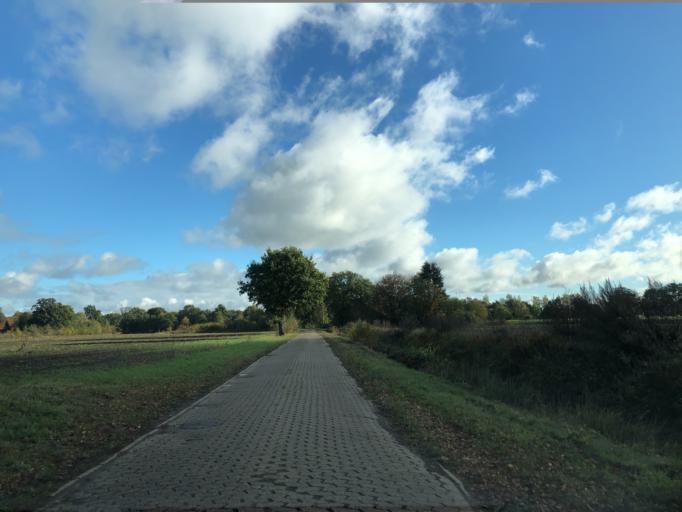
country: DE
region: Lower Saxony
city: Lehe
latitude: 53.0356
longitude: 7.3404
